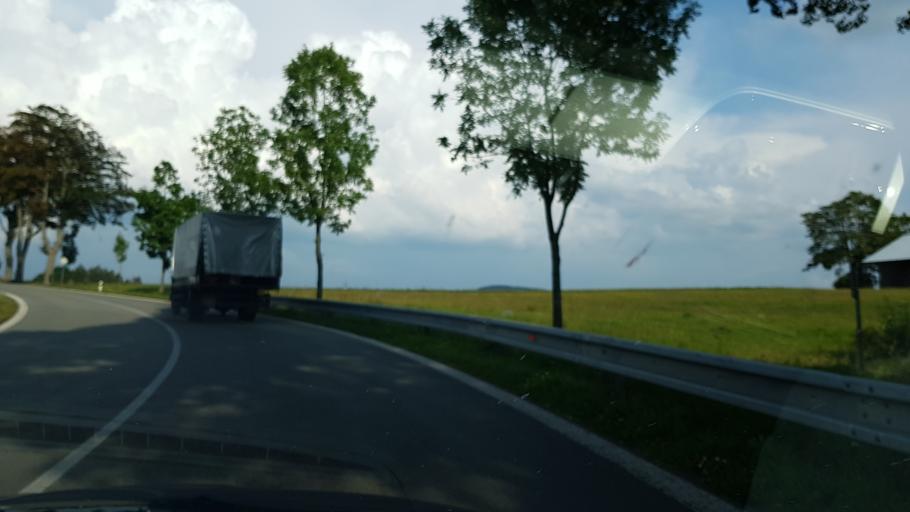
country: CZ
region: Pardubicky
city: Jablonne nad Orlici
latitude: 50.0874
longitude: 16.5990
